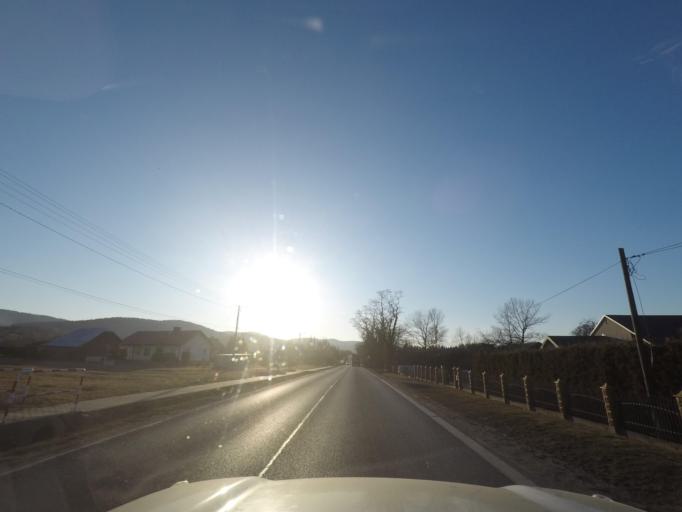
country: PL
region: Subcarpathian Voivodeship
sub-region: Powiat krosnienski
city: Dukla
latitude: 49.5580
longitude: 21.6351
